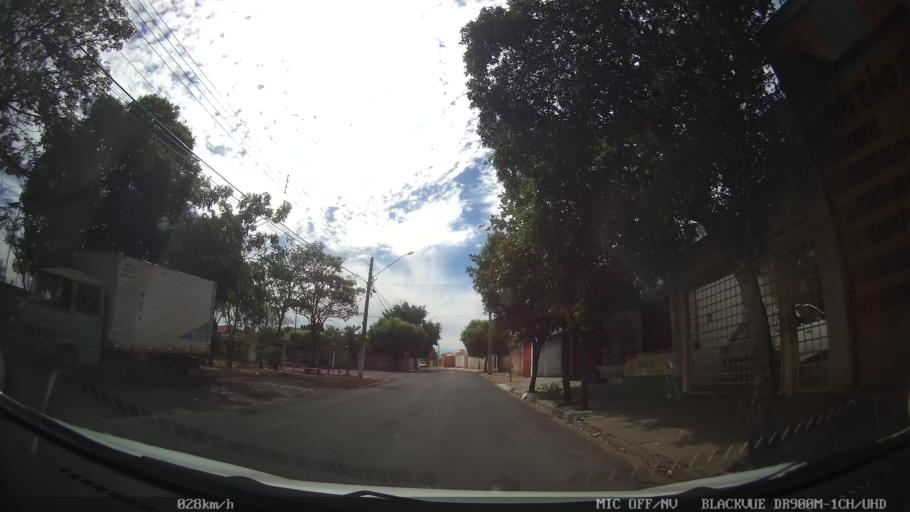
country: BR
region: Sao Paulo
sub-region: Catanduva
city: Catanduva
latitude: -21.1527
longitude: -48.9703
